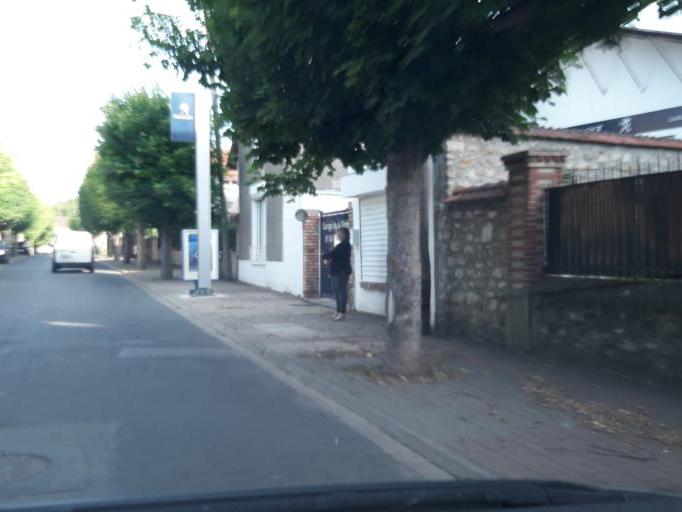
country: FR
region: Ile-de-France
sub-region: Departement de l'Essonne
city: Ballancourt-sur-Essonne
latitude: 48.5308
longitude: 2.3738
